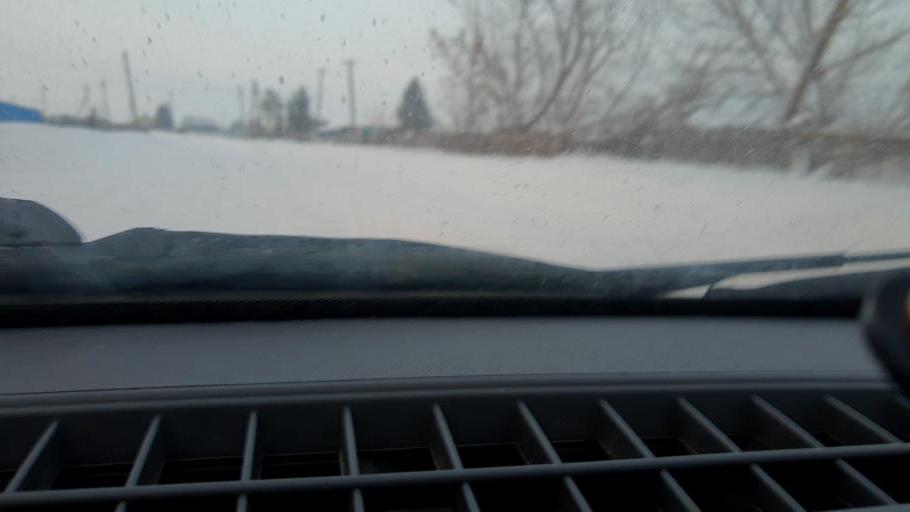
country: RU
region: Bashkortostan
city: Davlekanovo
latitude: 54.5448
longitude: 55.0377
